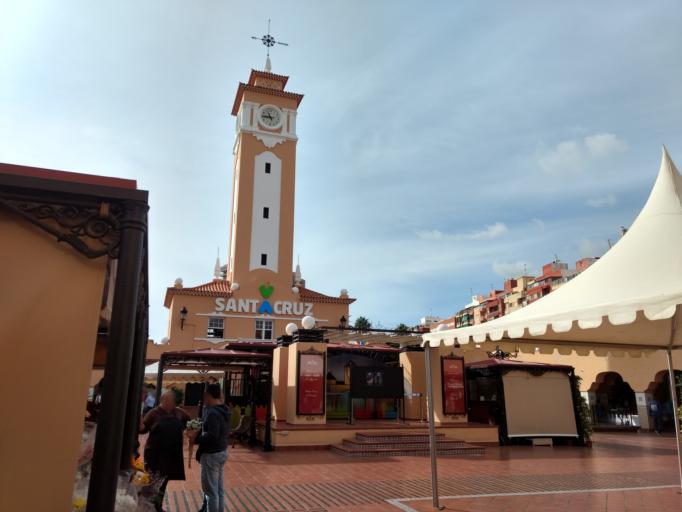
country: ES
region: Canary Islands
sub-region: Provincia de Santa Cruz de Tenerife
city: Santa Cruz de Tenerife
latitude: 28.4632
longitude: -16.2518
